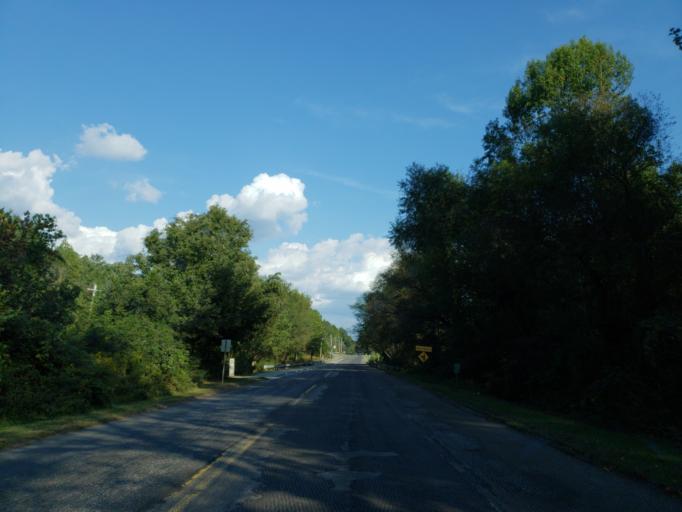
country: US
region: Georgia
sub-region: Cobb County
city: Powder Springs
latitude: 33.8644
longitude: -84.6946
